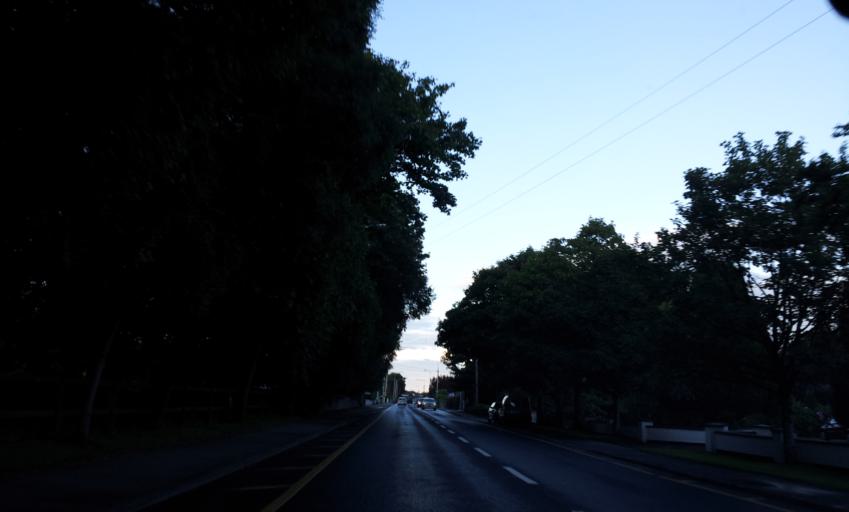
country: IE
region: Munster
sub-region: County Limerick
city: Newcastle West
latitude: 52.4458
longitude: -9.0706
